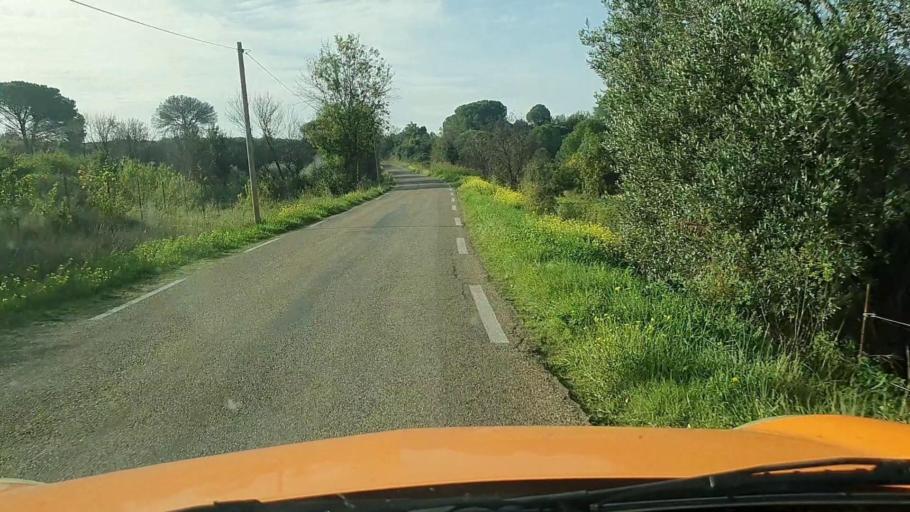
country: FR
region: Languedoc-Roussillon
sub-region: Departement du Gard
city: Generac
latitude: 43.7169
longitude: 4.3406
